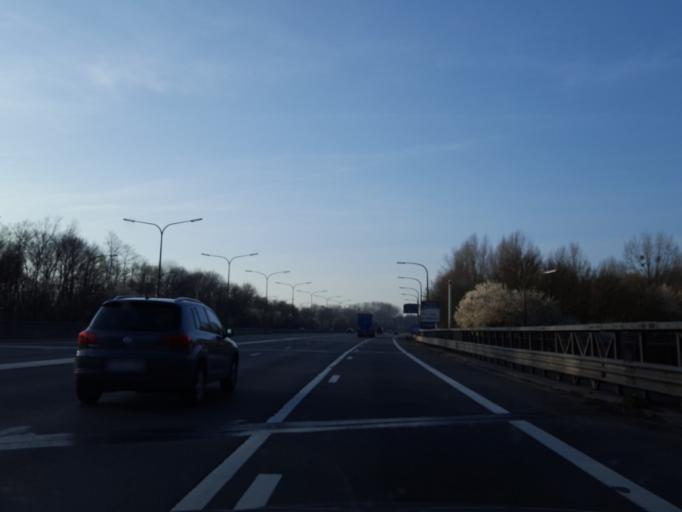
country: BE
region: Wallonia
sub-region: Province du Brabant Wallon
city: Nivelles
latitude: 50.5862
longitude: 4.3042
